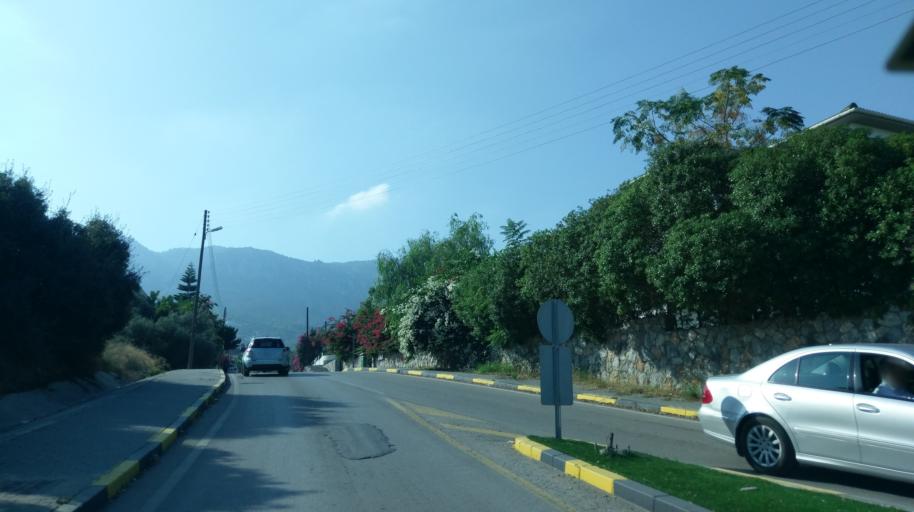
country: CY
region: Keryneia
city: Kyrenia
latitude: 35.3347
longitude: 33.2623
